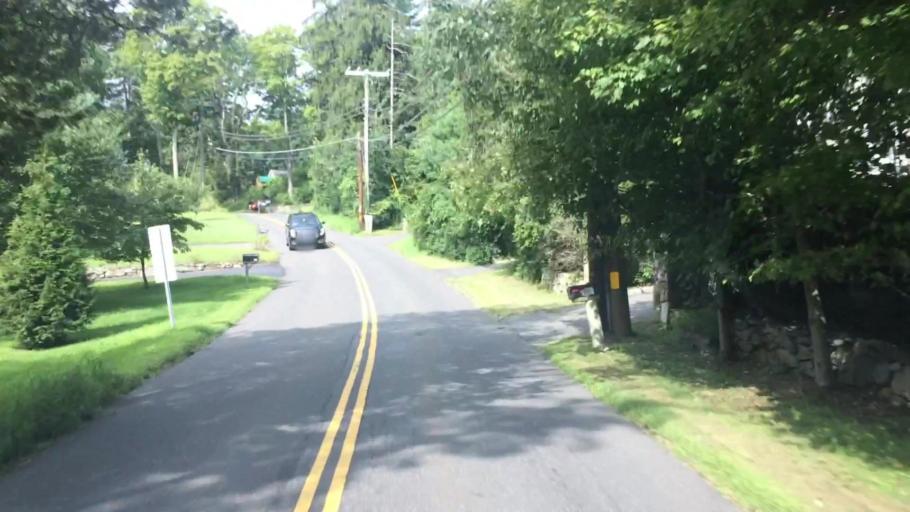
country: US
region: Connecticut
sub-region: Fairfield County
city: Danbury
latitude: 41.4068
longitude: -73.4881
